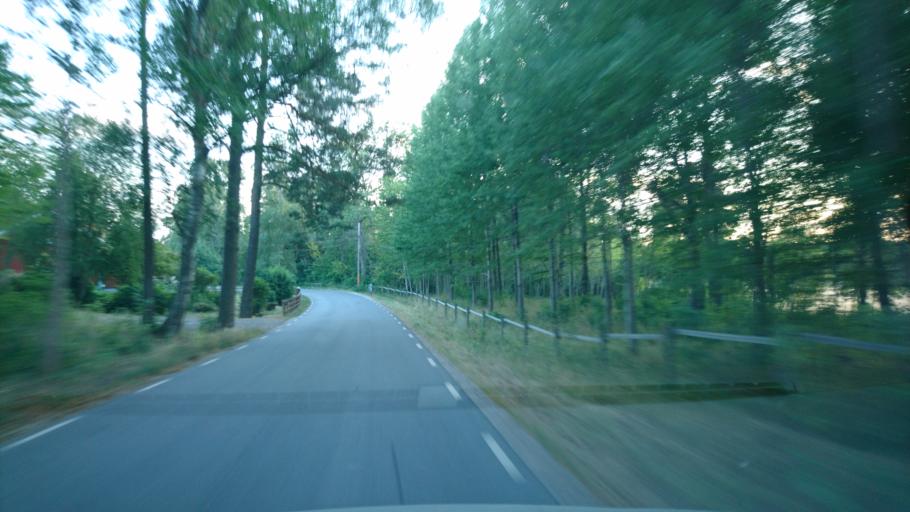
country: SE
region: Uppsala
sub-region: Uppsala Kommun
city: Saevja
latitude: 59.8104
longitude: 17.6791
